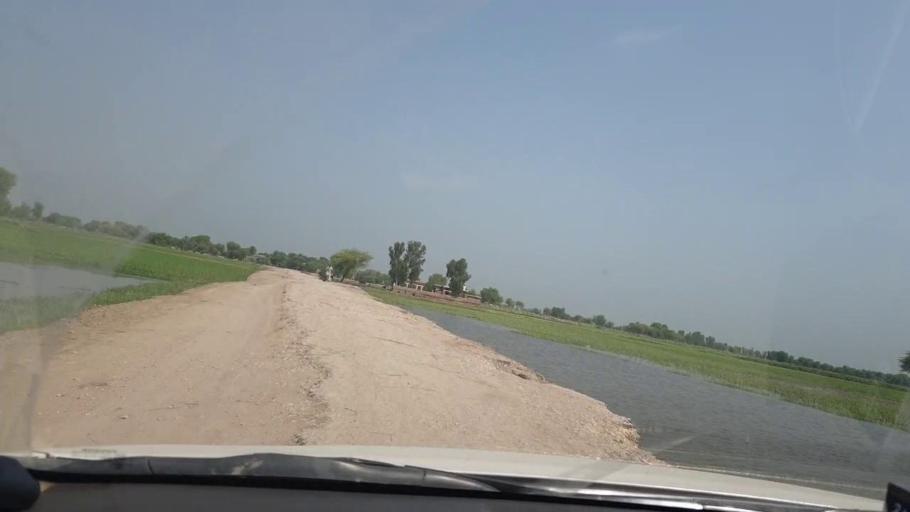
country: PK
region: Sindh
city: Chak
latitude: 27.8765
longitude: 68.7838
